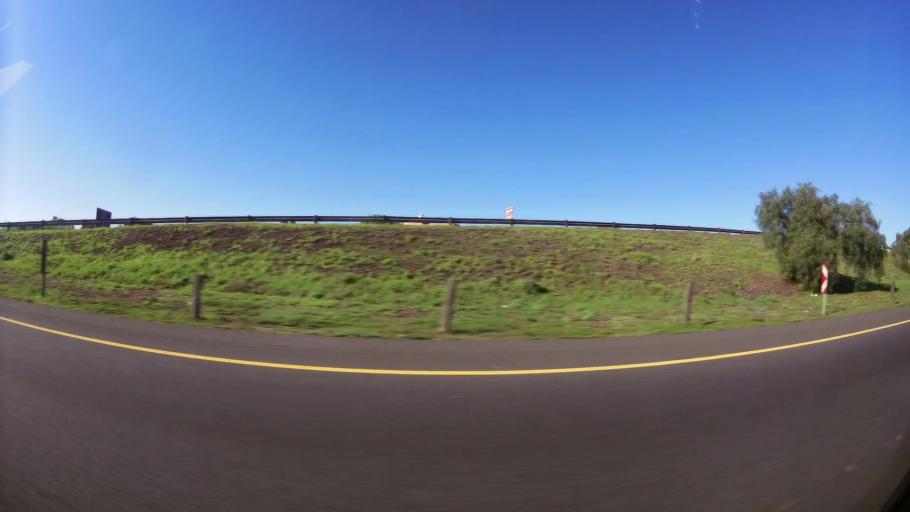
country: ZA
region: Eastern Cape
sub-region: Nelson Mandela Bay Metropolitan Municipality
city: Port Elizabeth
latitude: -33.9228
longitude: 25.5677
